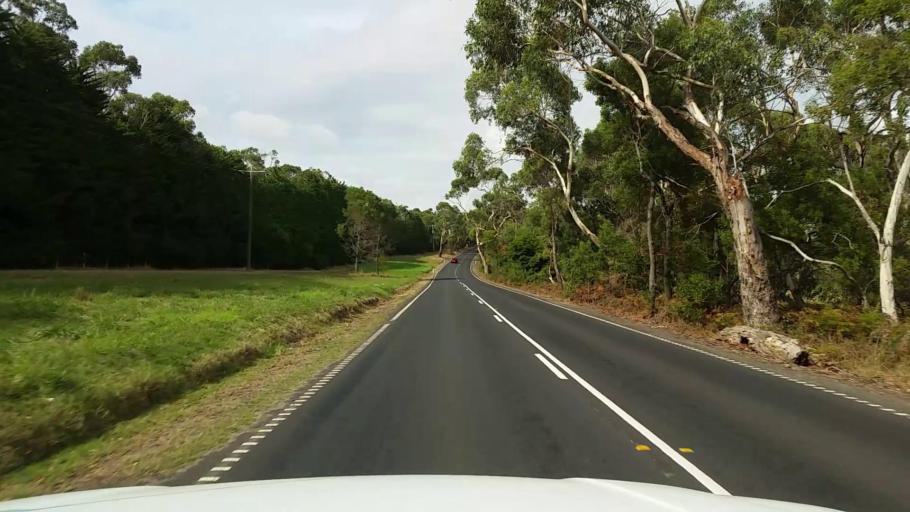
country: AU
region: Victoria
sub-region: Mornington Peninsula
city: Mount Martha
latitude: -38.3049
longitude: 145.0820
